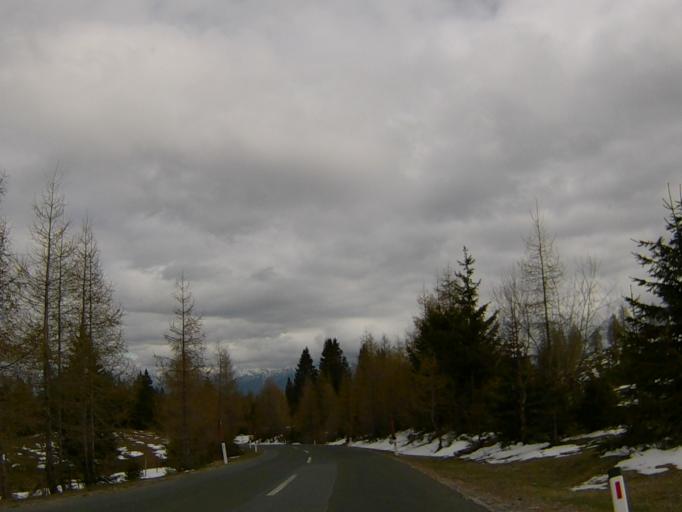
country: AT
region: Carinthia
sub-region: Politischer Bezirk Villach Land
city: Arnoldstein
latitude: 46.5947
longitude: 13.7185
